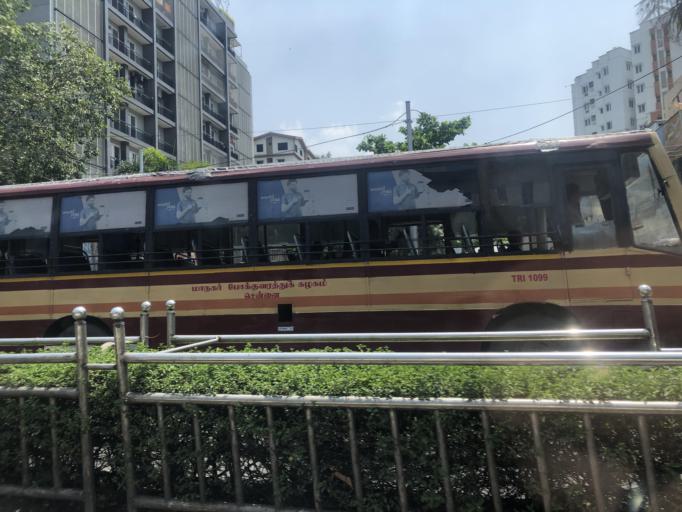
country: IN
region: Tamil Nadu
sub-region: Chennai
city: Gandhi Nagar
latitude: 12.9892
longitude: 80.2559
